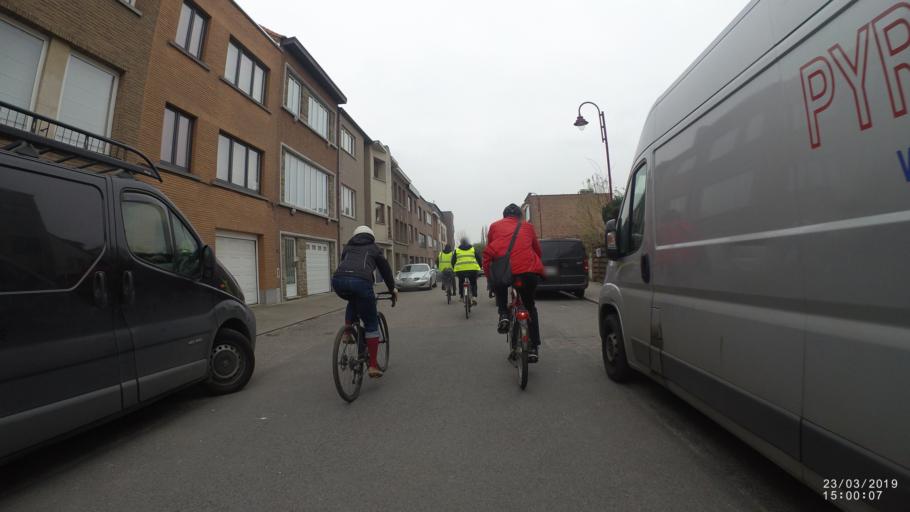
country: BE
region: Flanders
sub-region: Provincie Vlaams-Brabant
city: Dilbeek
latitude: 50.8563
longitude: 4.2933
